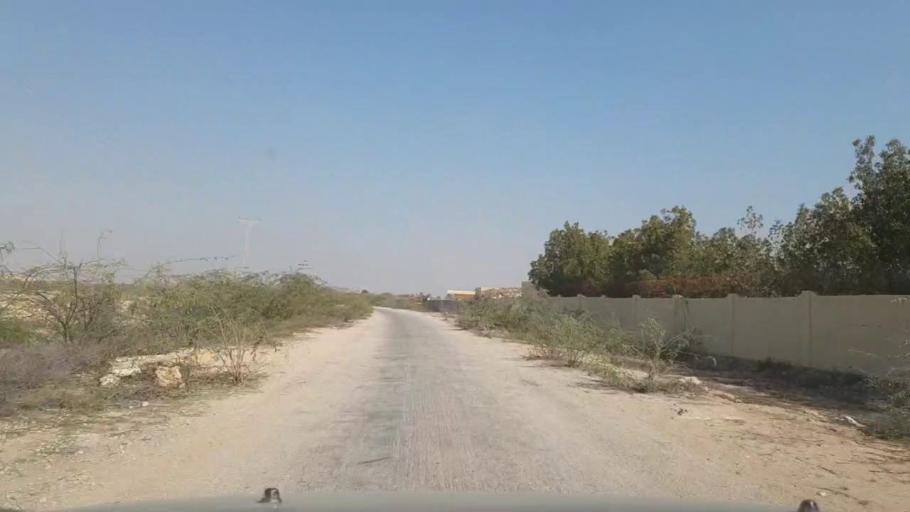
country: PK
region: Sindh
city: Thatta
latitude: 24.9957
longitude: 68.0092
